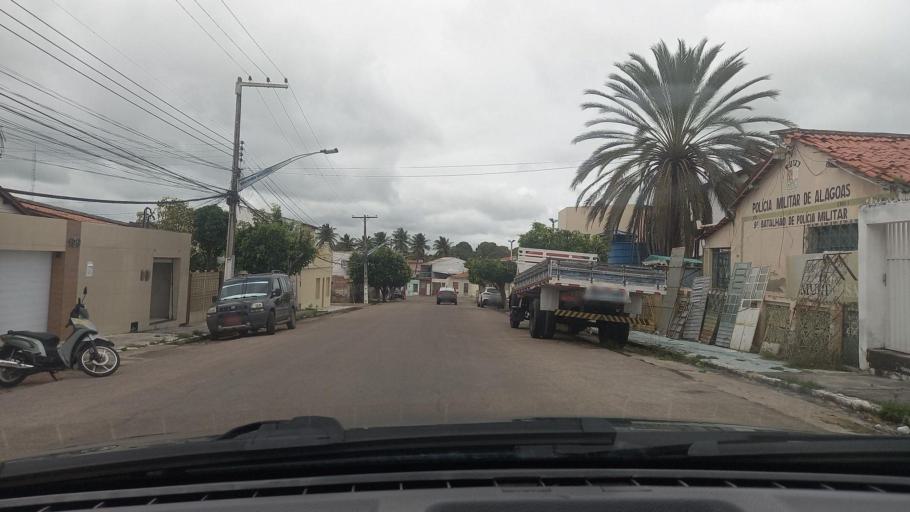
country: BR
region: Alagoas
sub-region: Delmiro Gouveia
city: Delmiro Gouveia
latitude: -9.3863
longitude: -37.9966
